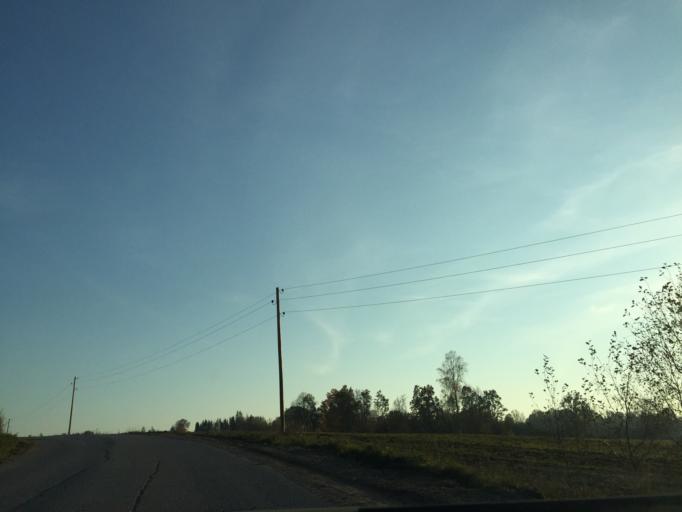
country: LV
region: Vainode
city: Vainode
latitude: 56.5559
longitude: 21.8401
